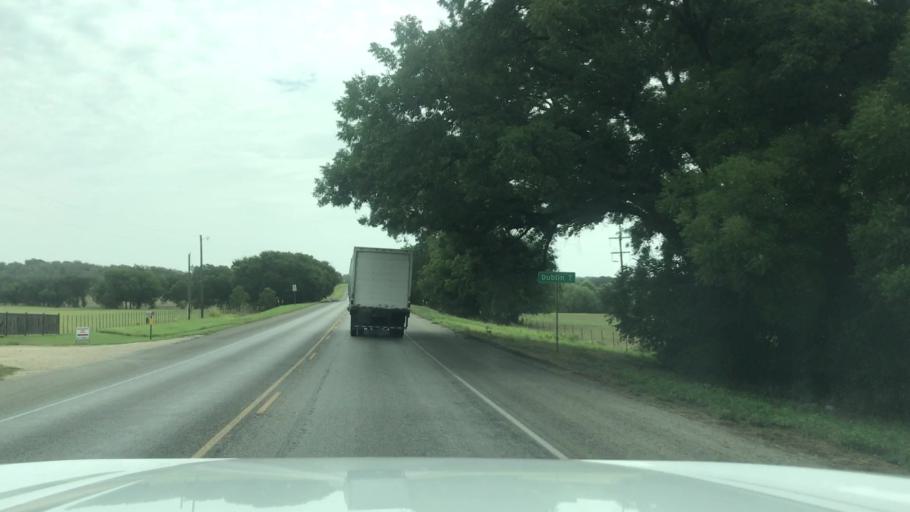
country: US
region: Texas
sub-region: Comanche County
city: De Leon
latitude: 32.0939
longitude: -98.4513
